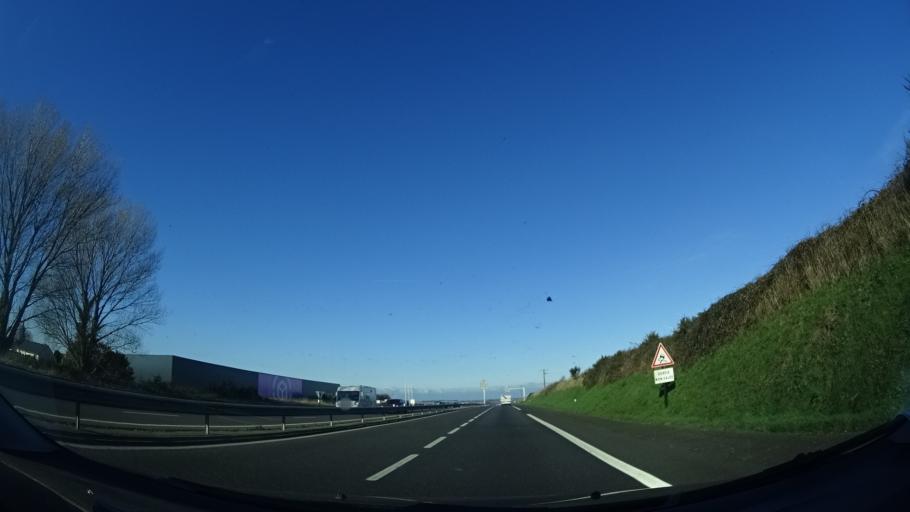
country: FR
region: Brittany
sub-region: Departement du Finistere
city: Henvic
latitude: 48.6320
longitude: -3.9213
